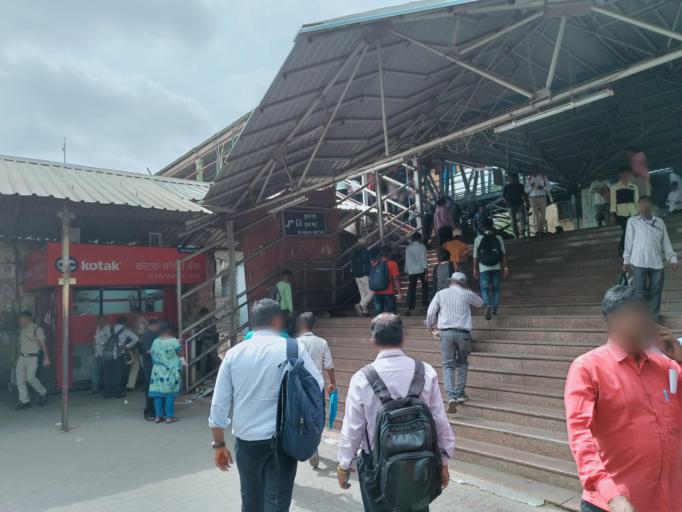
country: IN
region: Maharashtra
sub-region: Mumbai Suburban
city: Powai
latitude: 19.1197
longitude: 72.8486
